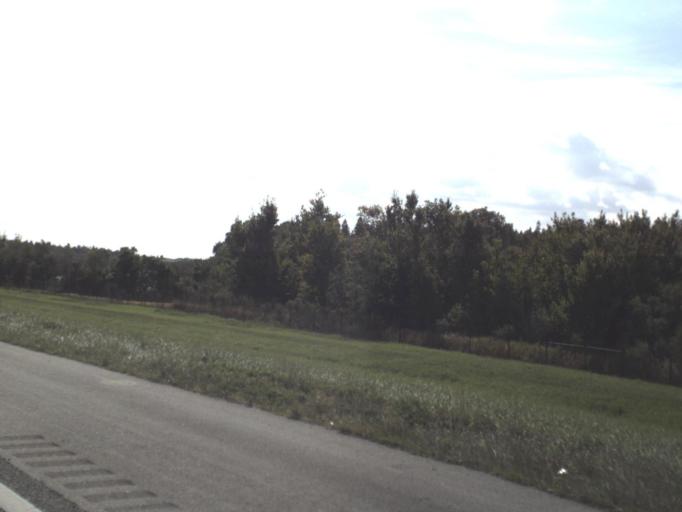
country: US
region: Florida
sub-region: Polk County
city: Winston
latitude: 28.0132
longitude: -82.0314
